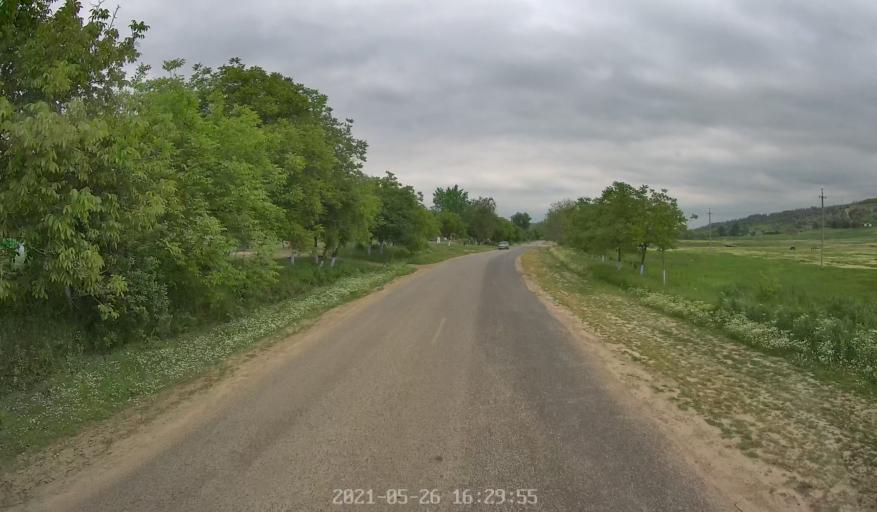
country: MD
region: Hincesti
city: Dancu
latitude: 46.7938
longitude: 28.3512
